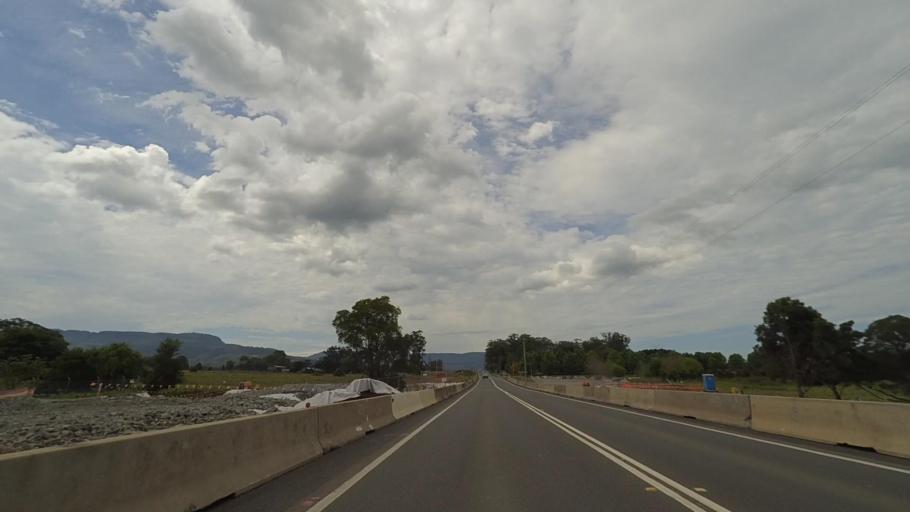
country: AU
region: New South Wales
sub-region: Shoalhaven Shire
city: Berry
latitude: -34.7862
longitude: 150.6756
